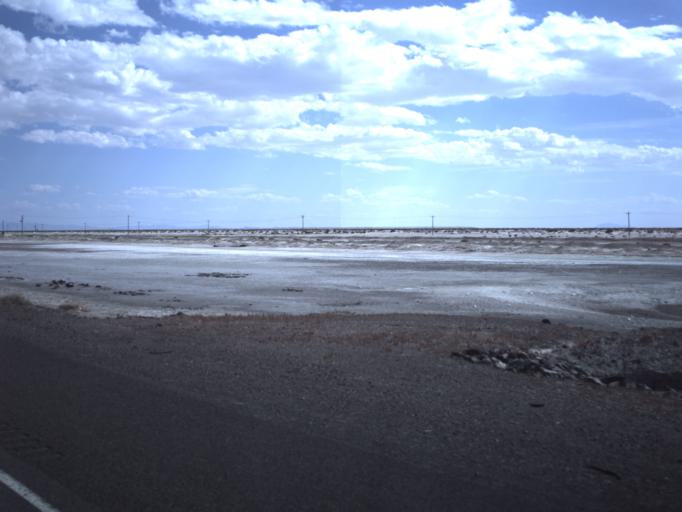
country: US
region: Utah
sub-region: Tooele County
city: Wendover
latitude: 40.7379
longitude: -113.8208
